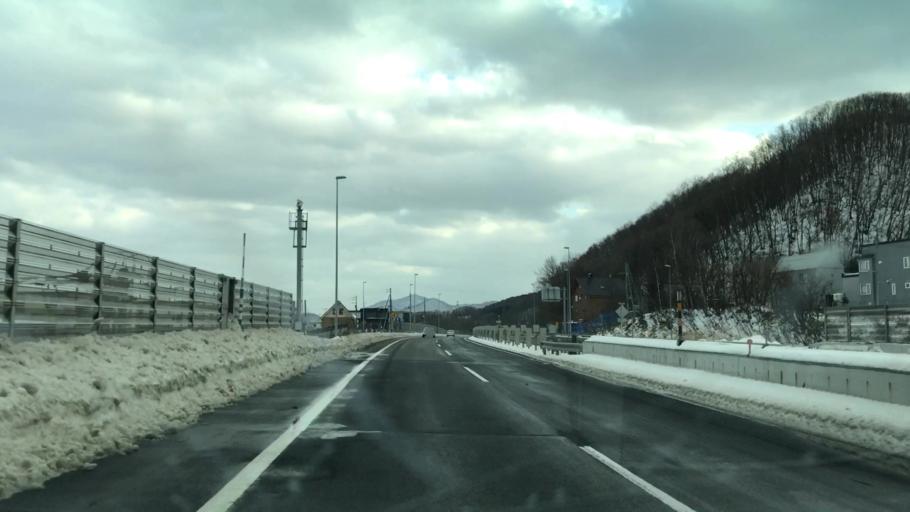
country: JP
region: Hokkaido
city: Sapporo
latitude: 43.1109
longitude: 141.2396
